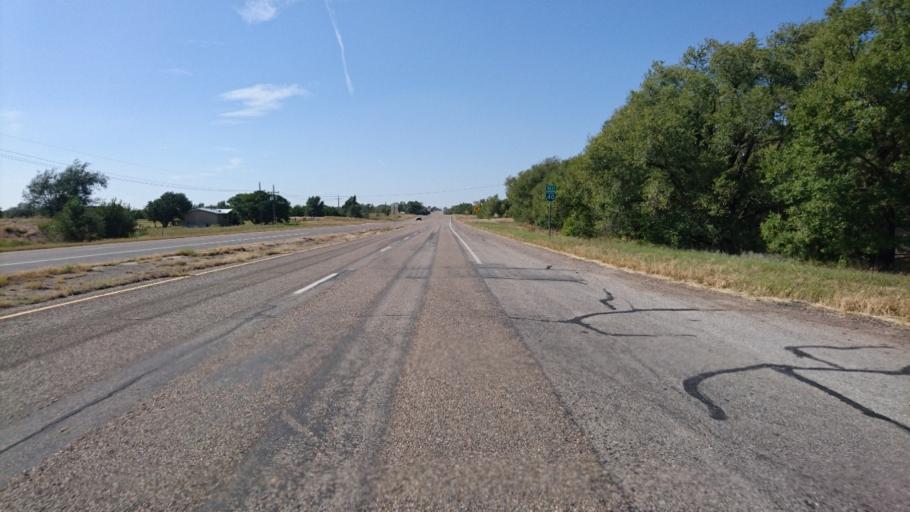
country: US
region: Texas
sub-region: Wheeler County
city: Shamrock
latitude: 35.2267
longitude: -100.2276
